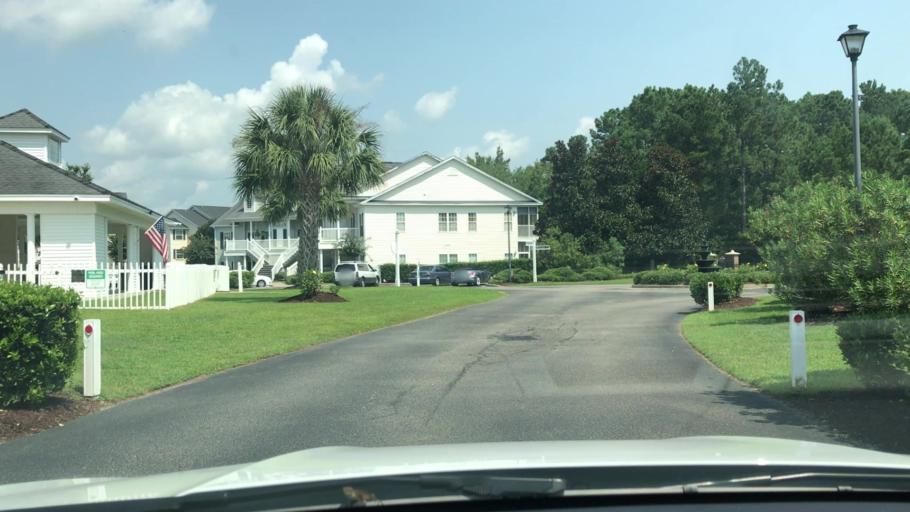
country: US
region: South Carolina
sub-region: Horry County
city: Forestbrook
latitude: 33.7781
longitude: -78.9651
